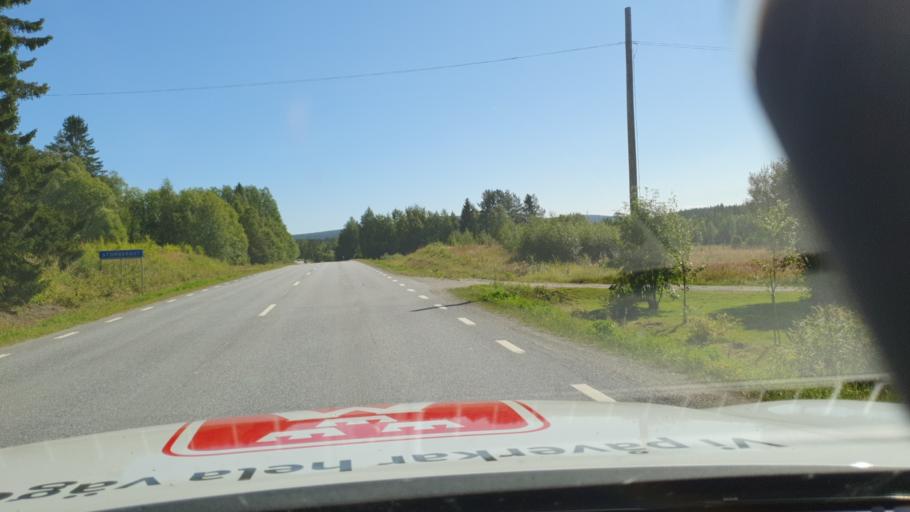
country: SE
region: Vaesterbotten
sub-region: Dorotea Kommun
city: Dorotea
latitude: 64.2550
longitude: 16.4540
